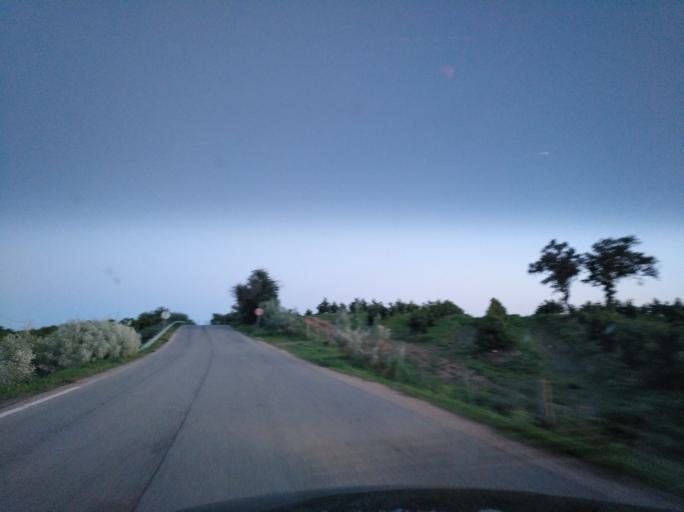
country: PT
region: Faro
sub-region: Vila Real de Santo Antonio
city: Monte Gordo
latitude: 37.1945
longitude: -7.5154
